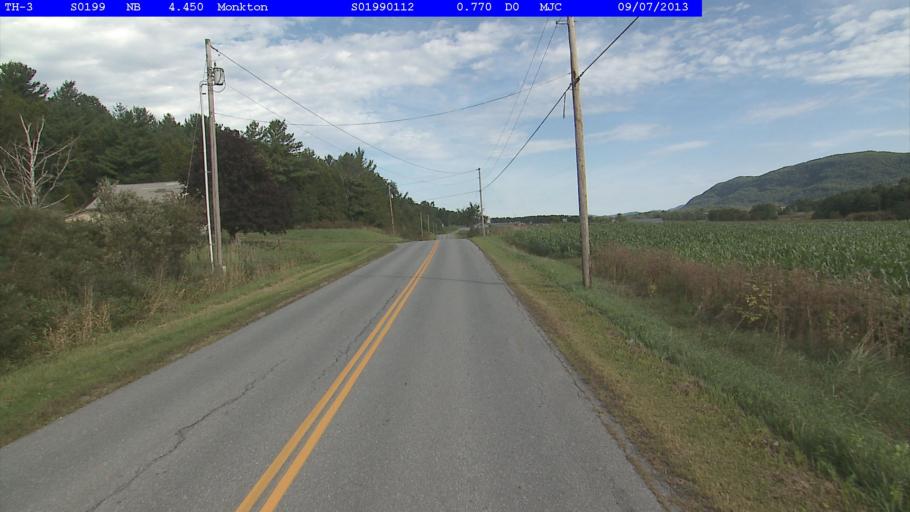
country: US
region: Vermont
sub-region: Addison County
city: Bristol
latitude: 44.1917
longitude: -73.1088
